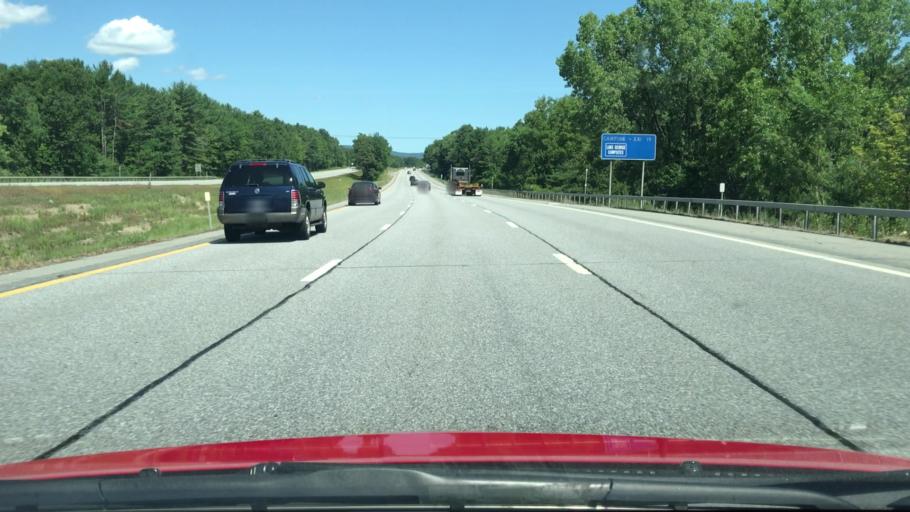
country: US
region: New York
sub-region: Warren County
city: Glens Falls North
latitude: 43.3188
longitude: -73.6762
